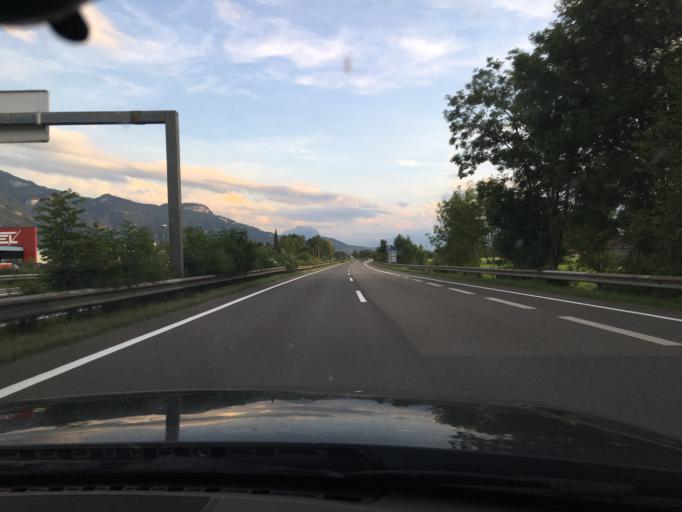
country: AT
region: Vorarlberg
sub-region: Politischer Bezirk Dornbirn
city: Dornbirn
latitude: 47.4105
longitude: 9.7061
